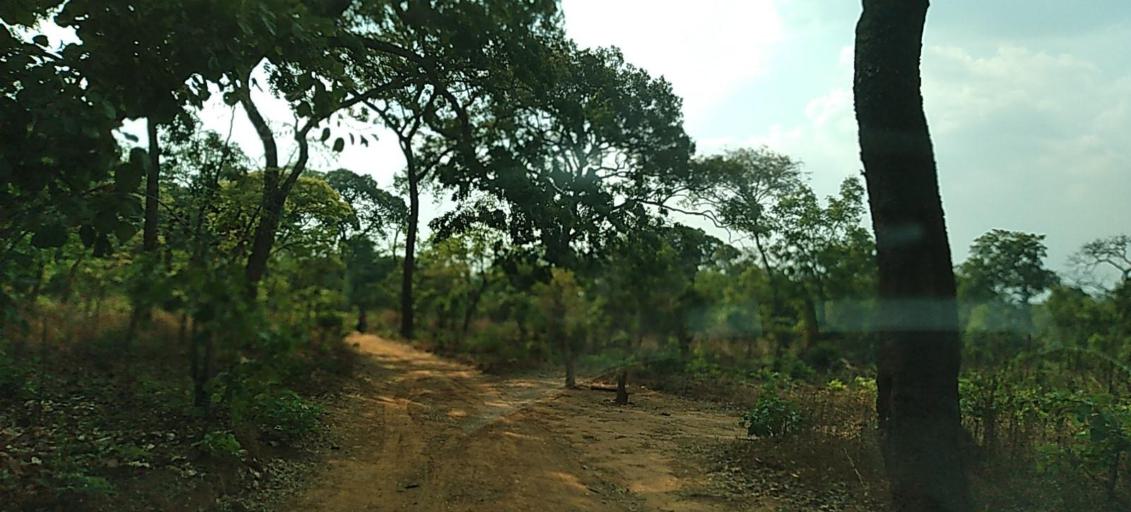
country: ZM
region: North-Western
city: Solwezi
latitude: -12.0663
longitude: 26.2152
